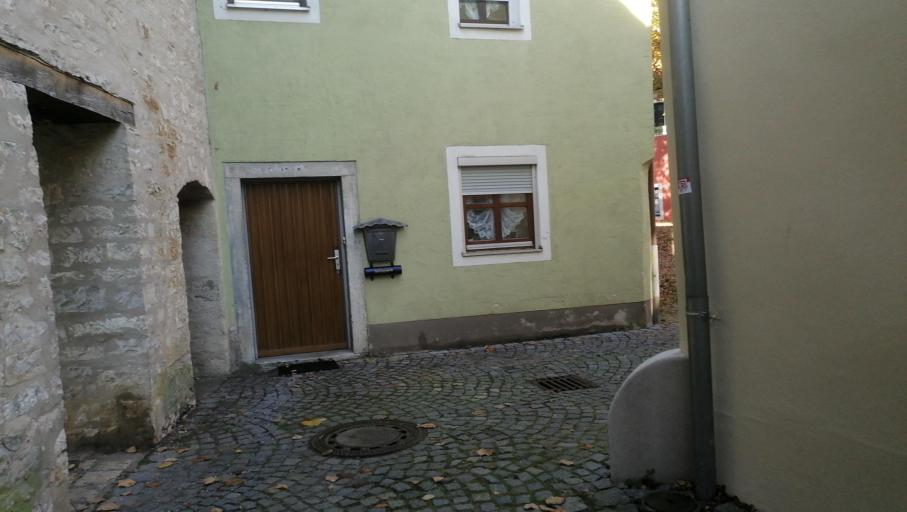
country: DE
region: Bavaria
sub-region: Upper Palatinate
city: Berching
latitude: 49.1057
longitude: 11.4390
